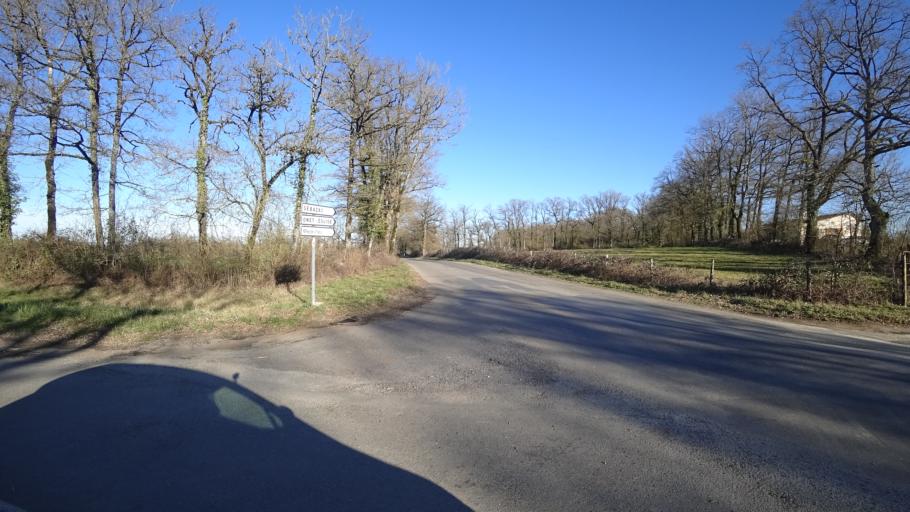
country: FR
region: Midi-Pyrenees
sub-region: Departement de l'Aveyron
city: Sebazac-Concoures
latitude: 44.4092
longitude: 2.5623
